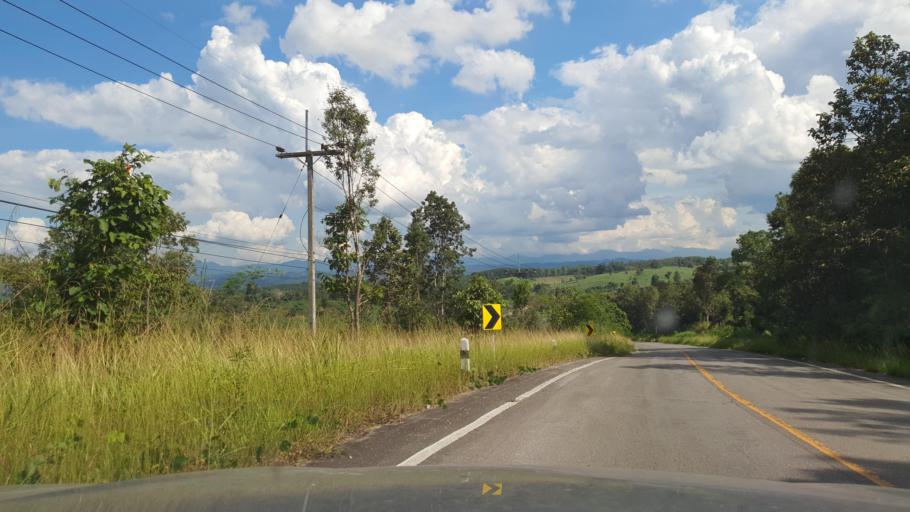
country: TH
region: Chiang Rai
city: Wiang Pa Pao
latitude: 19.3309
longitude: 99.4656
